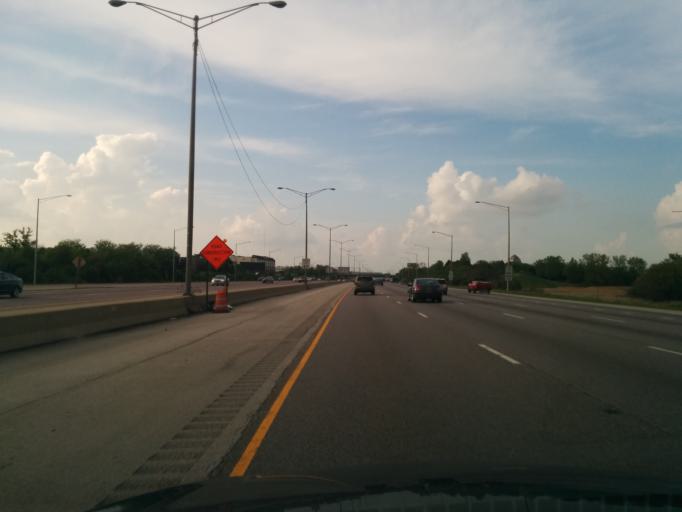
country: US
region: Illinois
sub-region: DuPage County
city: Itasca
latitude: 41.9661
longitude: -88.0256
